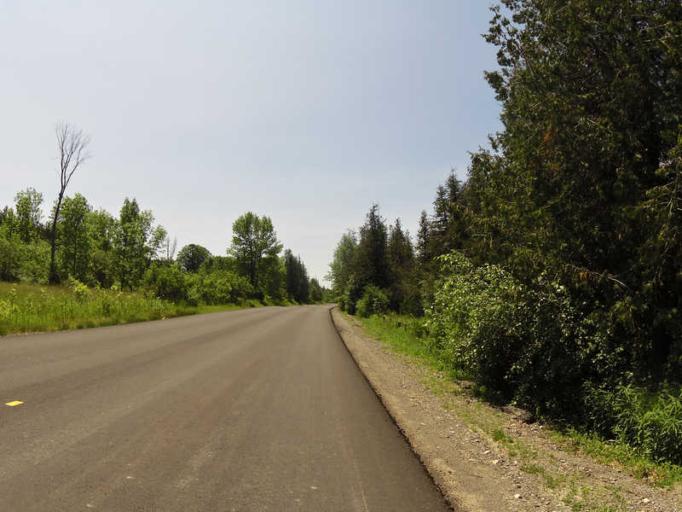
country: CA
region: Ontario
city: Peterborough
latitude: 44.3762
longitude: -78.2834
